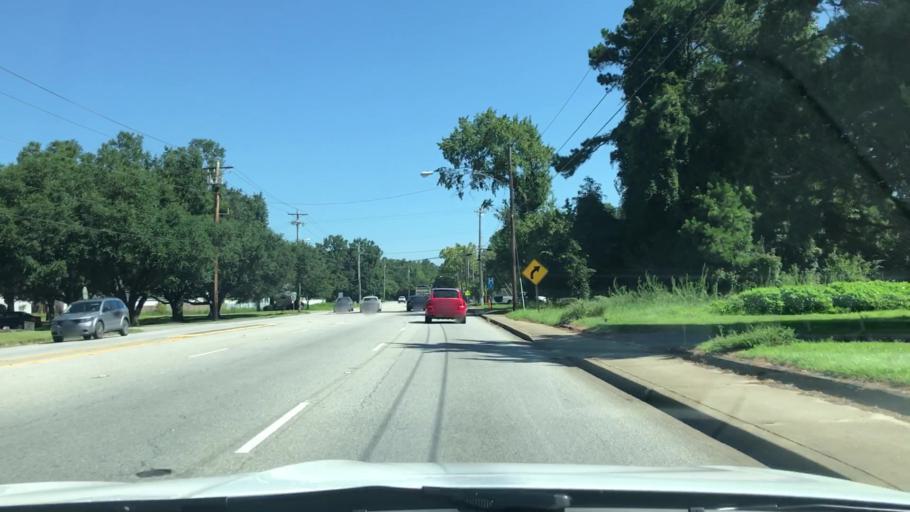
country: US
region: South Carolina
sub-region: Horry County
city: Conway
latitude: 33.8176
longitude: -79.0777
